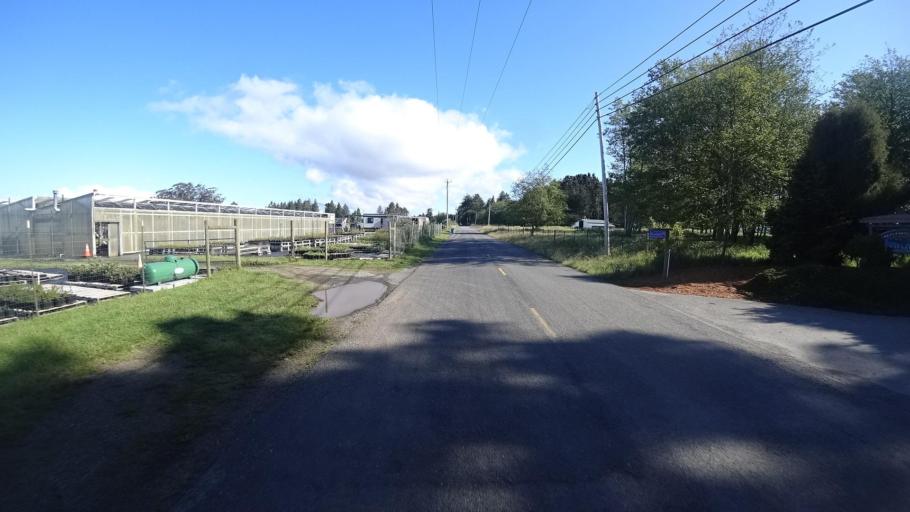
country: US
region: California
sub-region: Humboldt County
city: Westhaven-Moonstone
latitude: 41.0004
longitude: -124.1005
